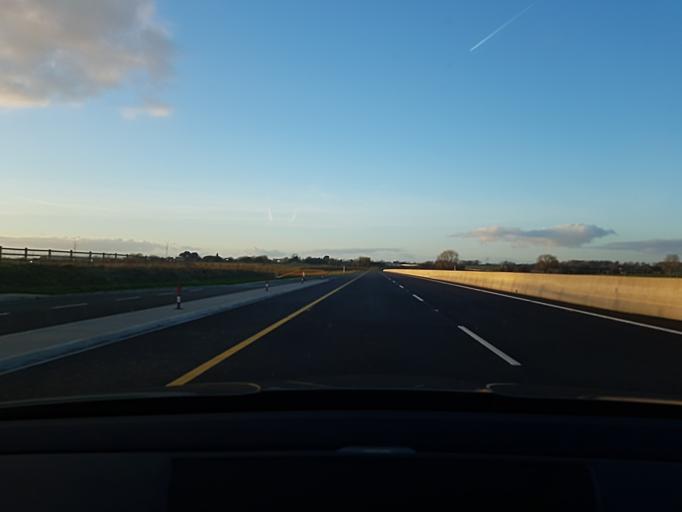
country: IE
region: Connaught
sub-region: County Galway
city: Tuam
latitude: 53.4286
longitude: -8.8372
